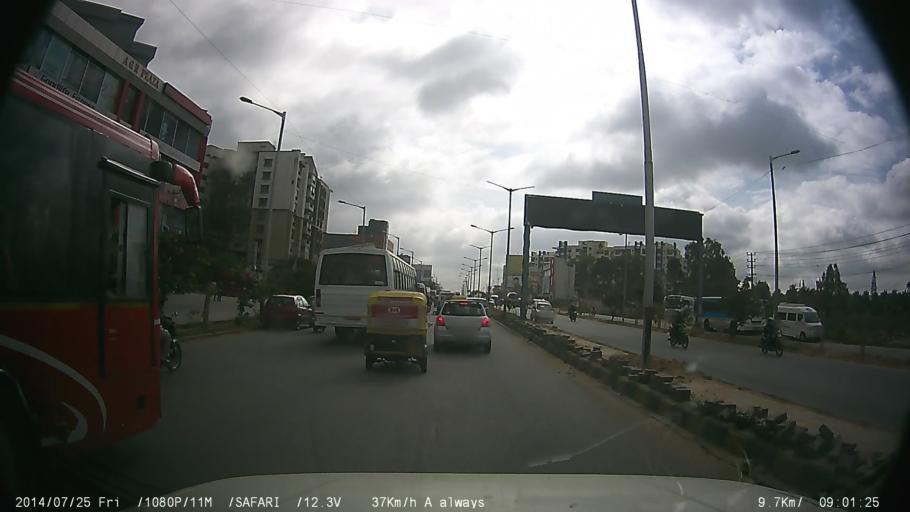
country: IN
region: Karnataka
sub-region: Bangalore Urban
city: Bangalore
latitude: 12.9220
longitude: 77.6680
